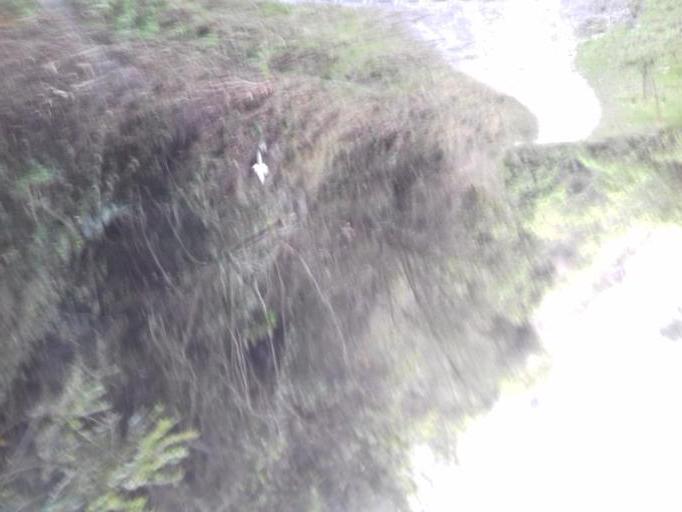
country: CO
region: Tolima
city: Cajamarca
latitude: 4.5343
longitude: -75.4599
